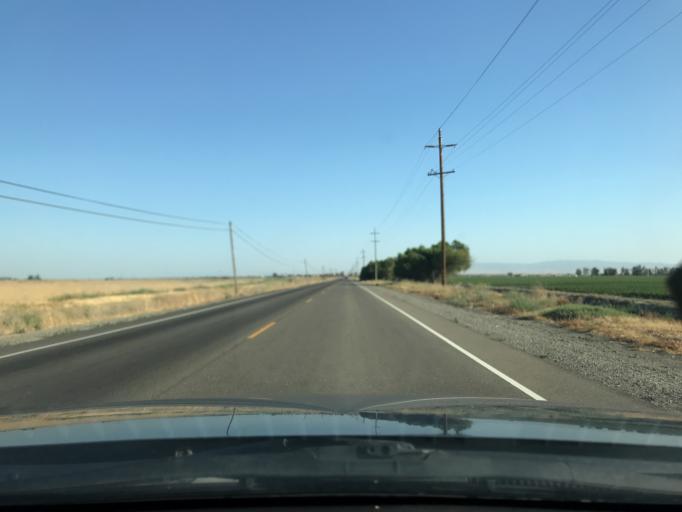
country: US
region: California
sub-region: Merced County
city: Los Banos
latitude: 37.1205
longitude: -120.8348
